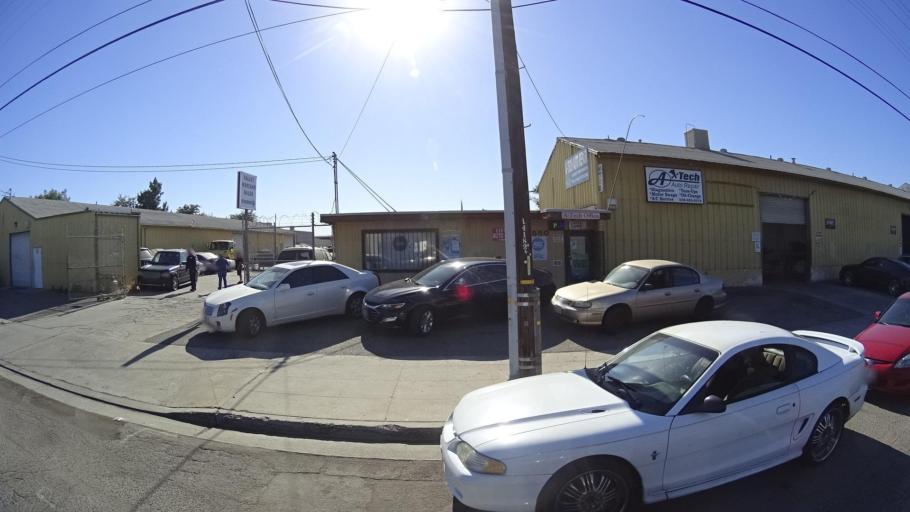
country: US
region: California
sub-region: Fresno County
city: Fresno
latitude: 36.7638
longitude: -119.7861
